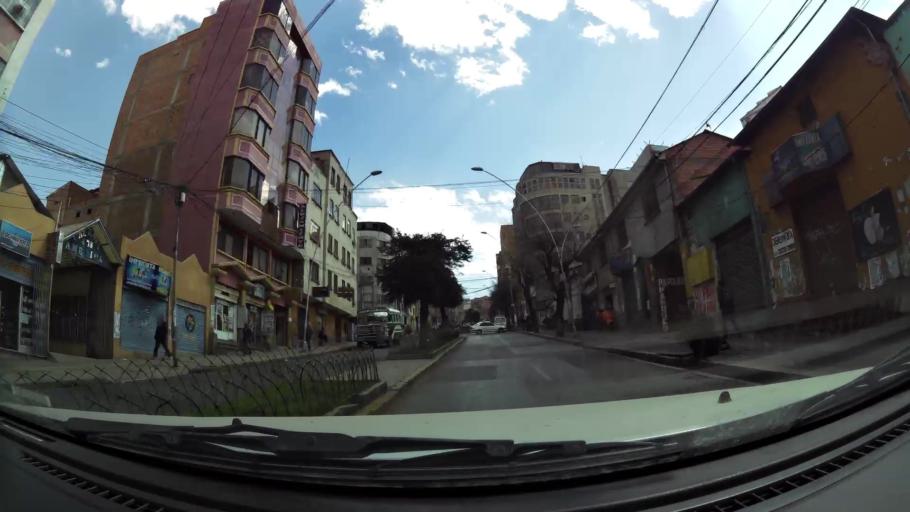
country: BO
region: La Paz
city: La Paz
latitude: -16.4932
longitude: -68.1414
